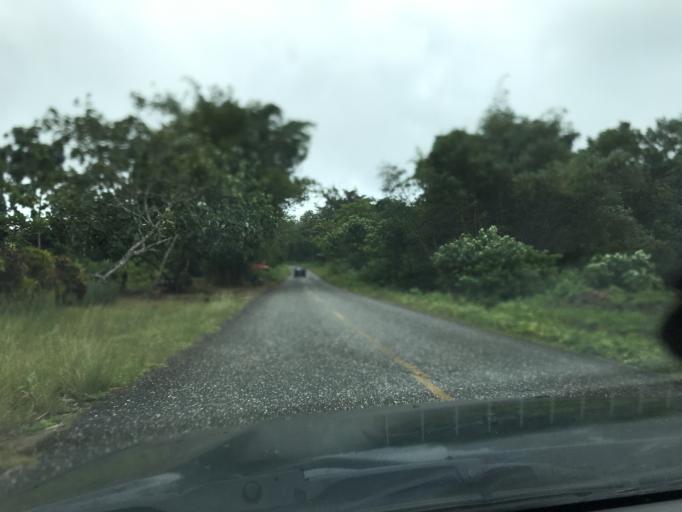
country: SB
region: Western Province
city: Gizo
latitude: -8.2441
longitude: 157.2356
